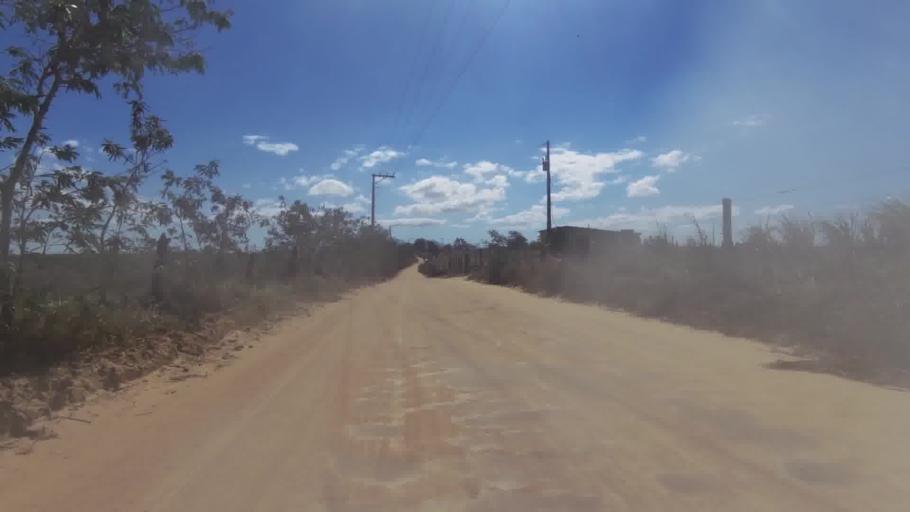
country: BR
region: Espirito Santo
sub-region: Marataizes
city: Marataizes
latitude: -21.1621
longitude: -40.9748
